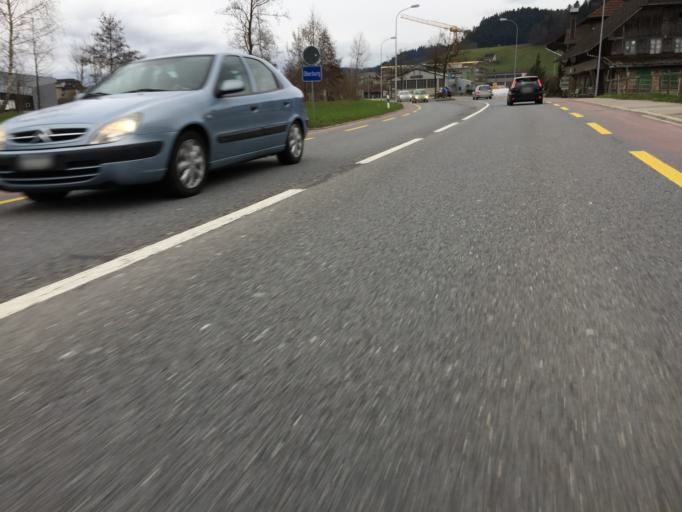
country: CH
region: Bern
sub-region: Emmental District
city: Oberburg
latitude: 47.0430
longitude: 7.6225
